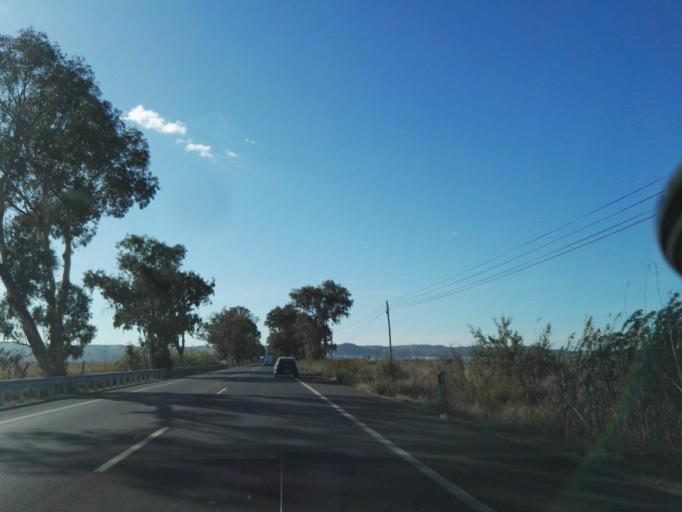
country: PT
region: Santarem
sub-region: Benavente
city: Samora Correia
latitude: 38.9373
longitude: -8.9300
